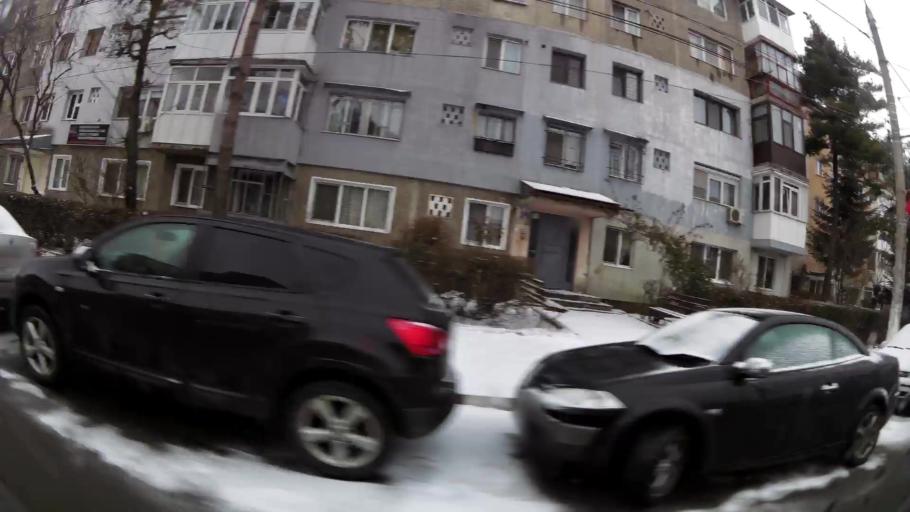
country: RO
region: Dambovita
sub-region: Municipiul Targoviste
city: Targoviste
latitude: 44.9206
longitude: 25.4678
